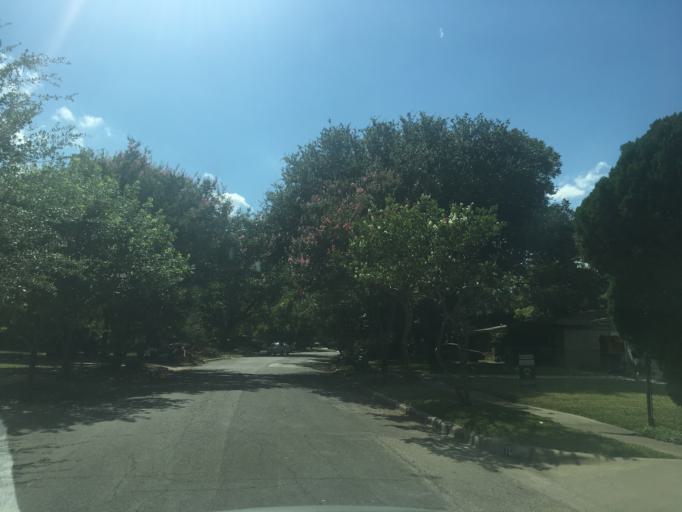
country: US
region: Texas
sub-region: Dallas County
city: Garland
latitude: 32.8364
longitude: -96.6830
